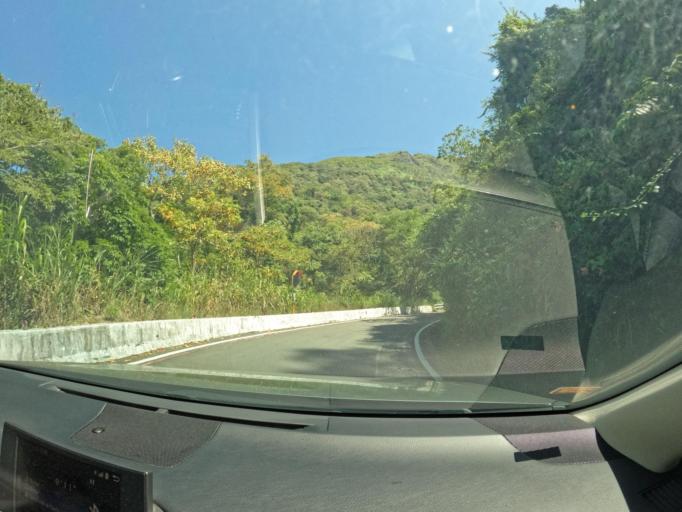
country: TW
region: Taiwan
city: Yujing
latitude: 23.2738
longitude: 120.8466
